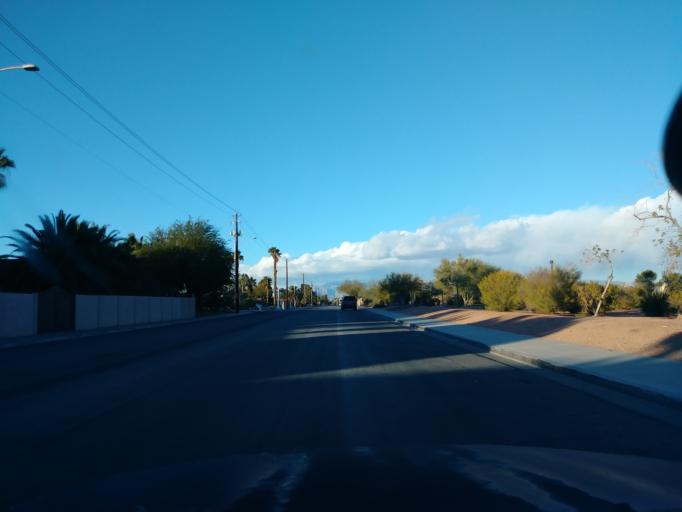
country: US
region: Nevada
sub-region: Clark County
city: Spring Valley
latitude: 36.1483
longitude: -115.2386
